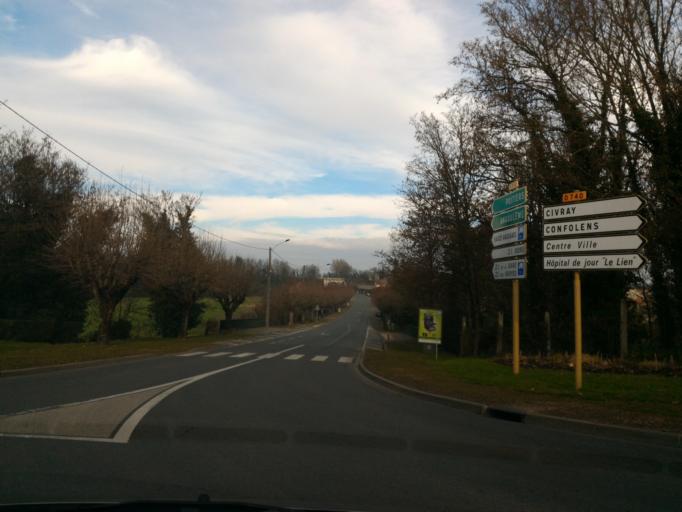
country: FR
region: Poitou-Charentes
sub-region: Departement de la Charente
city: Ruffec
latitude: 46.0298
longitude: 0.1972
